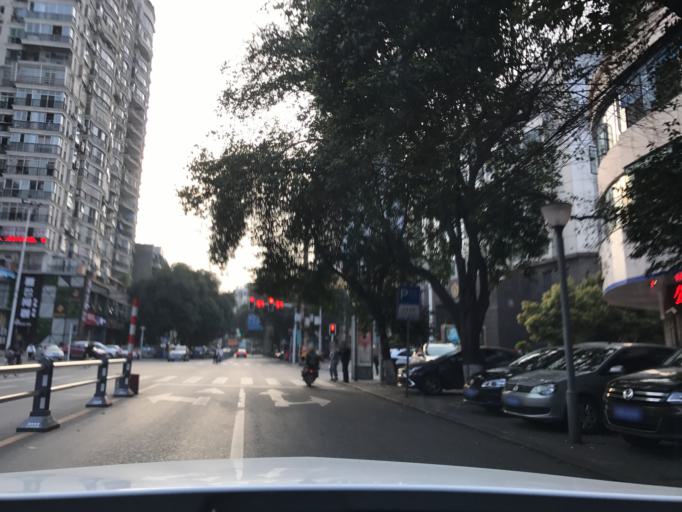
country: CN
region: Sichuan
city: Mianyang
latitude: 31.4548
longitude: 104.7498
